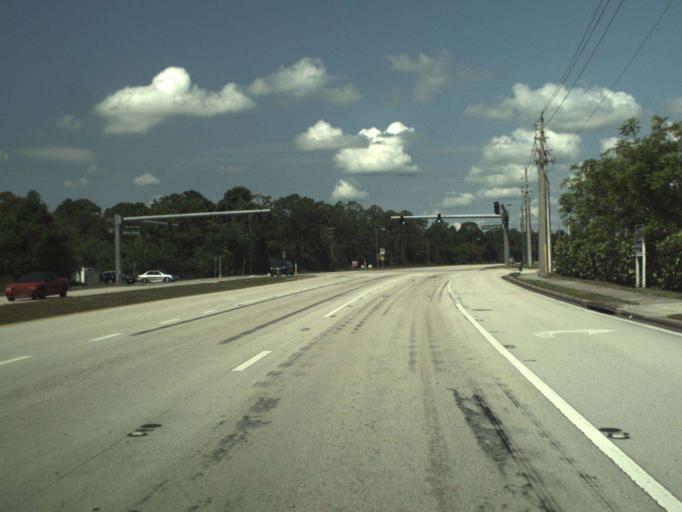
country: US
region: Florida
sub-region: Brevard County
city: June Park
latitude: 28.1219
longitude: -80.6930
